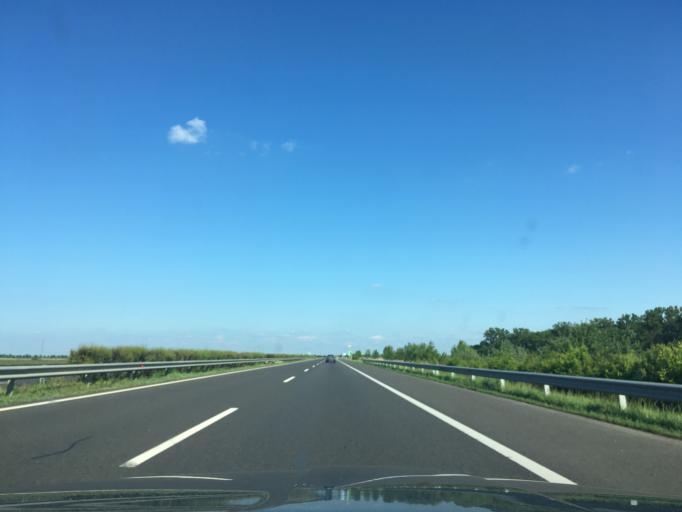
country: HU
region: Hajdu-Bihar
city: Gorbehaza
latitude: 47.8036
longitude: 21.1850
